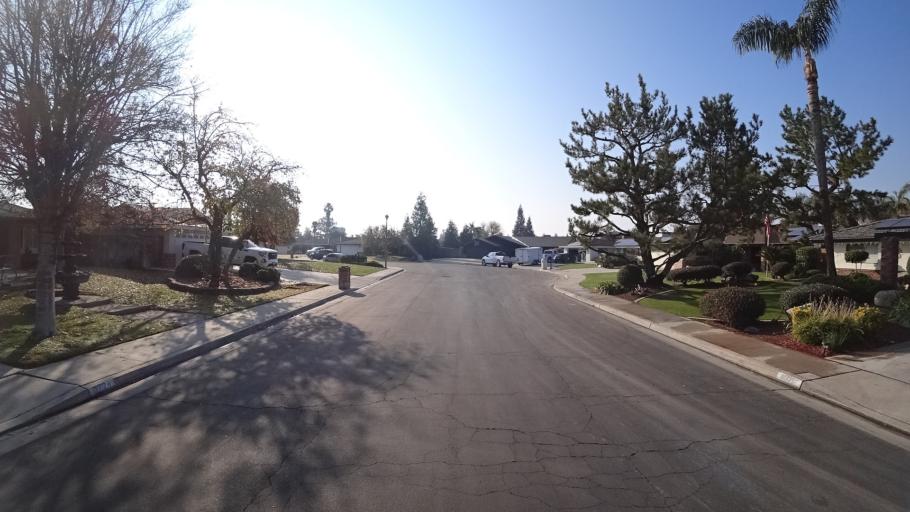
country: US
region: California
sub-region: Kern County
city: Greenacres
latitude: 35.3393
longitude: -119.0777
